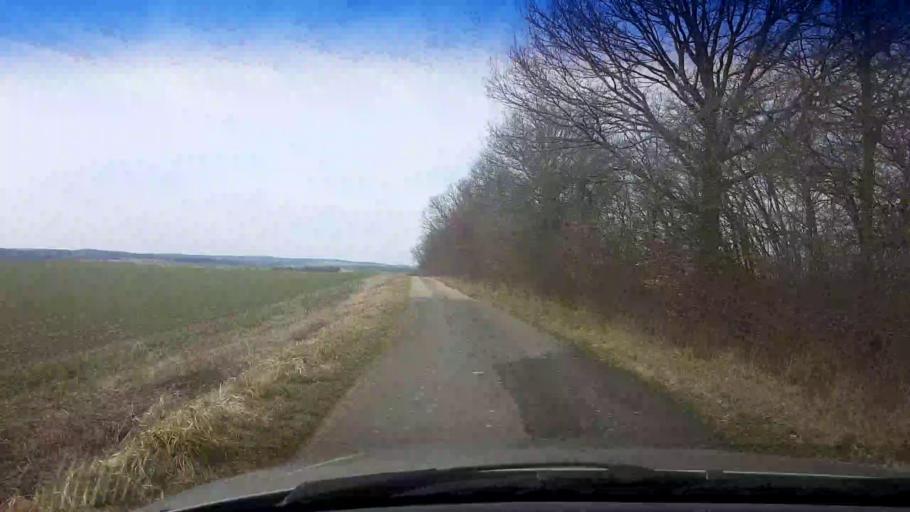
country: DE
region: Bavaria
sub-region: Upper Franconia
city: Burgebrach
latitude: 49.8119
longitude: 10.7596
